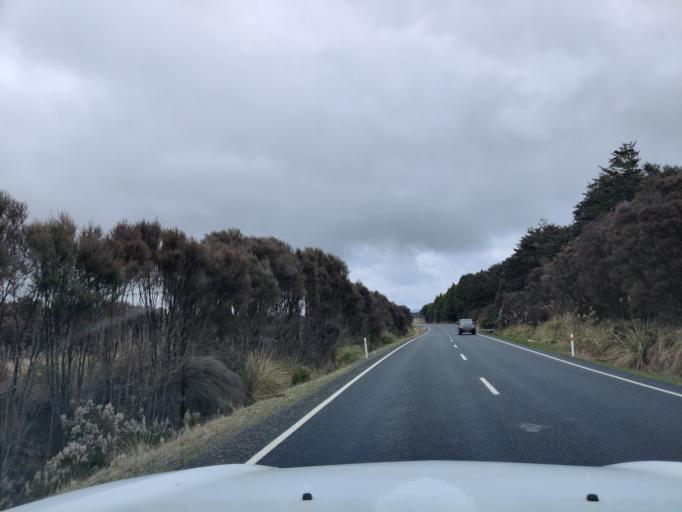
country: NZ
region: Manawatu-Wanganui
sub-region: Ruapehu District
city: Waiouru
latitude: -39.3332
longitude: 175.3810
